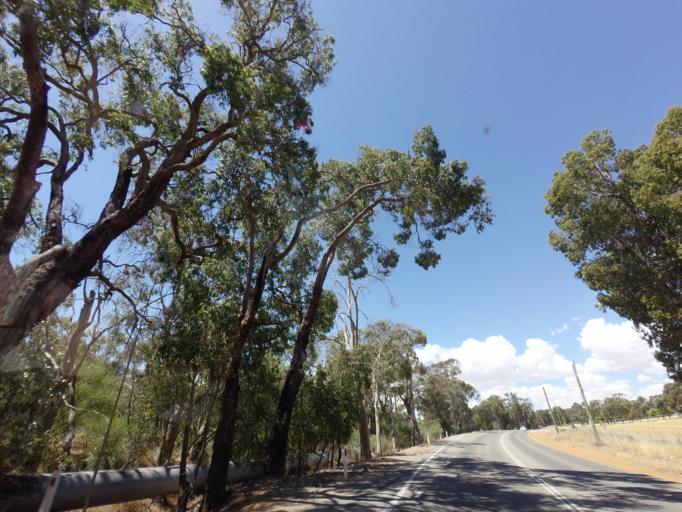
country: AU
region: Western Australia
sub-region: Northam
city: Wundowie
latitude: -31.7579
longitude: 116.4377
